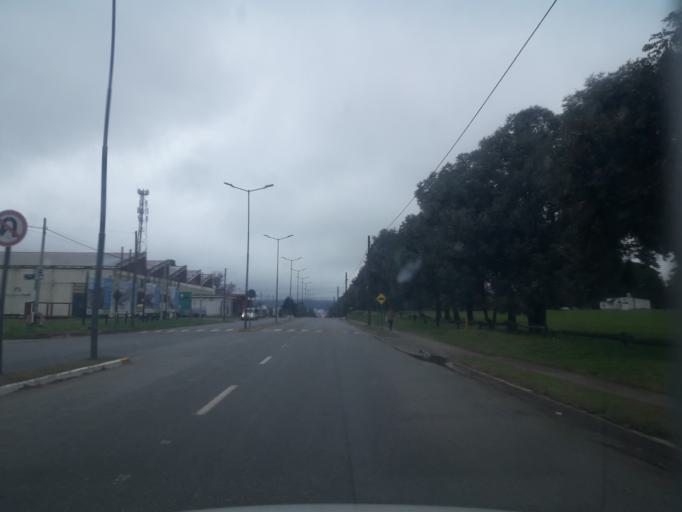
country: AR
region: Buenos Aires
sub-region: Partido de Tandil
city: Tandil
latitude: -37.3022
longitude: -59.1684
